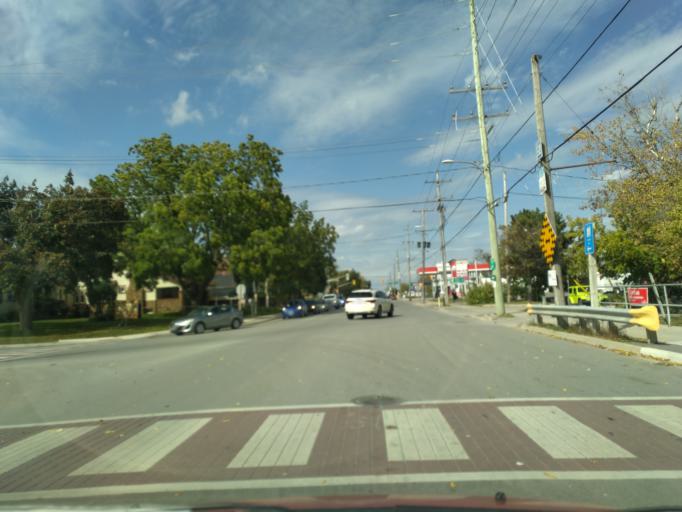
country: CA
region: Ontario
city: Keswick
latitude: 44.3033
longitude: -79.3623
